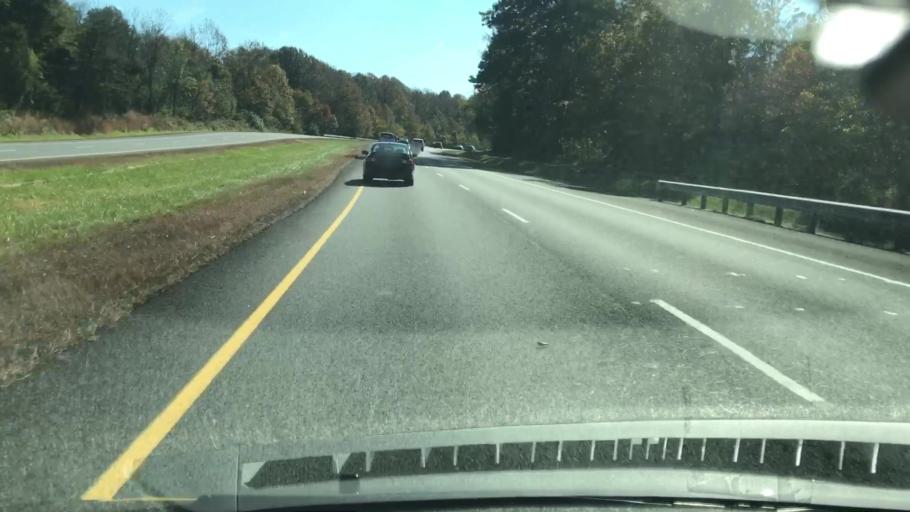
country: US
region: Virginia
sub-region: Fairfax County
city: Fairfax Station
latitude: 38.8149
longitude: -77.3453
